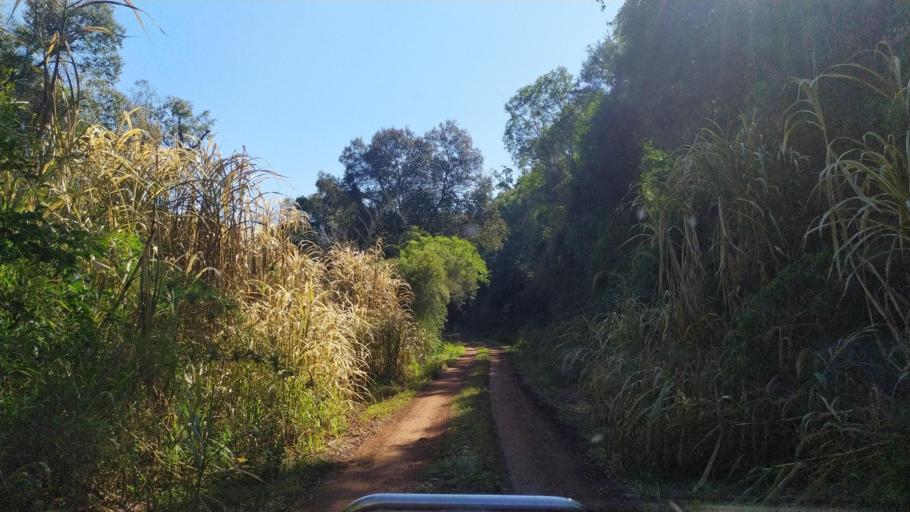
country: AR
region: Misiones
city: El Alcazar
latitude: -26.7533
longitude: -54.6009
